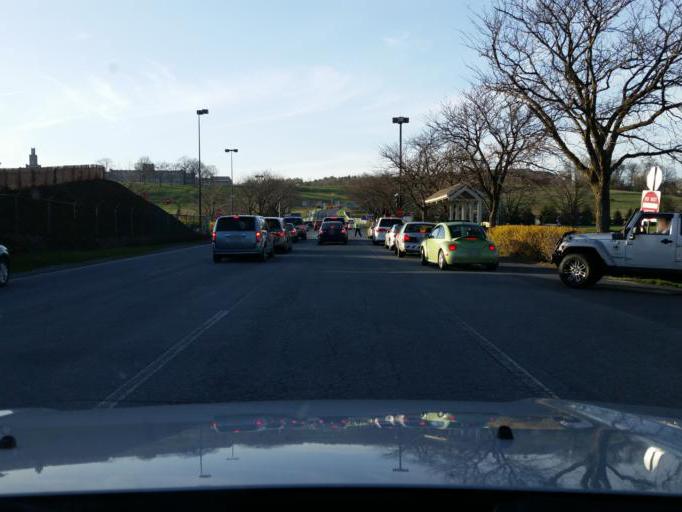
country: US
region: Pennsylvania
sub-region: Dauphin County
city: Hershey
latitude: 40.2909
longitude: -76.6582
